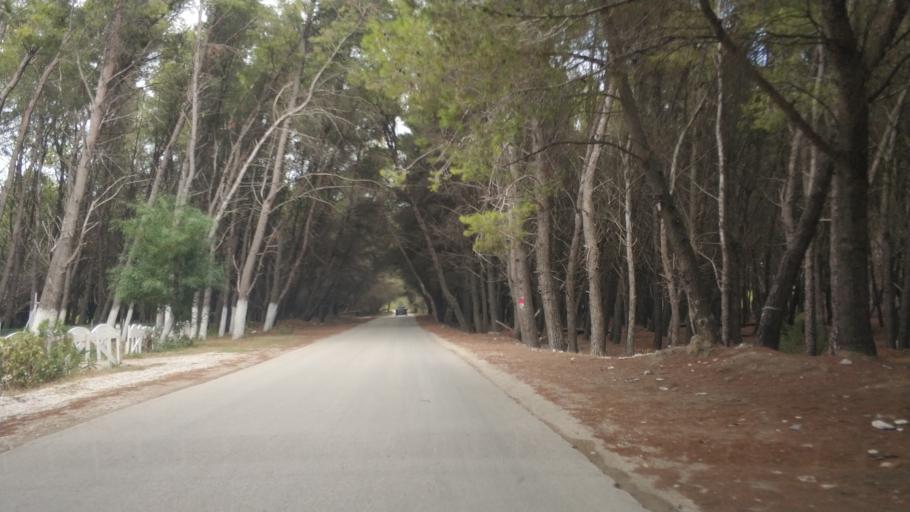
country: AL
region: Vlore
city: Vlore
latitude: 40.4888
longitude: 19.4414
